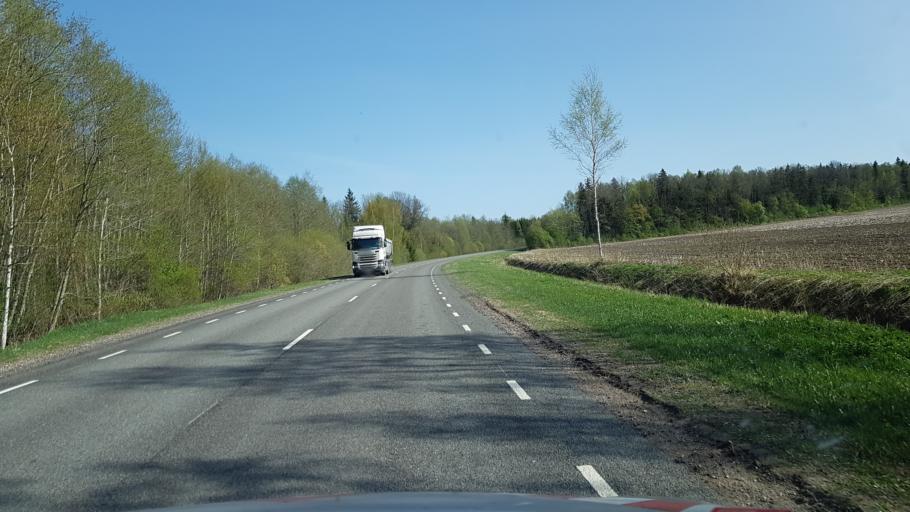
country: EE
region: Viljandimaa
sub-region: Karksi vald
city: Karksi-Nuia
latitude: 58.2056
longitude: 25.5367
